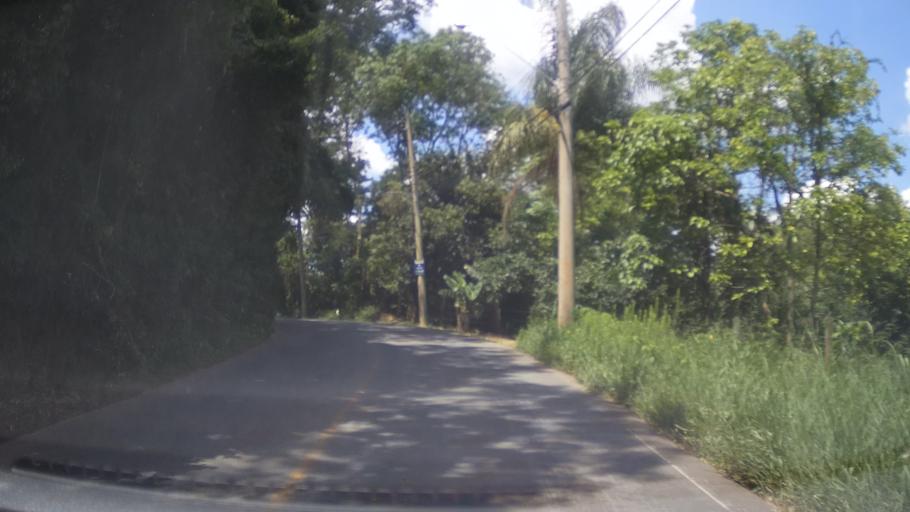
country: BR
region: Sao Paulo
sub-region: Varzea Paulista
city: Varzea Paulista
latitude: -23.1402
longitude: -46.8176
